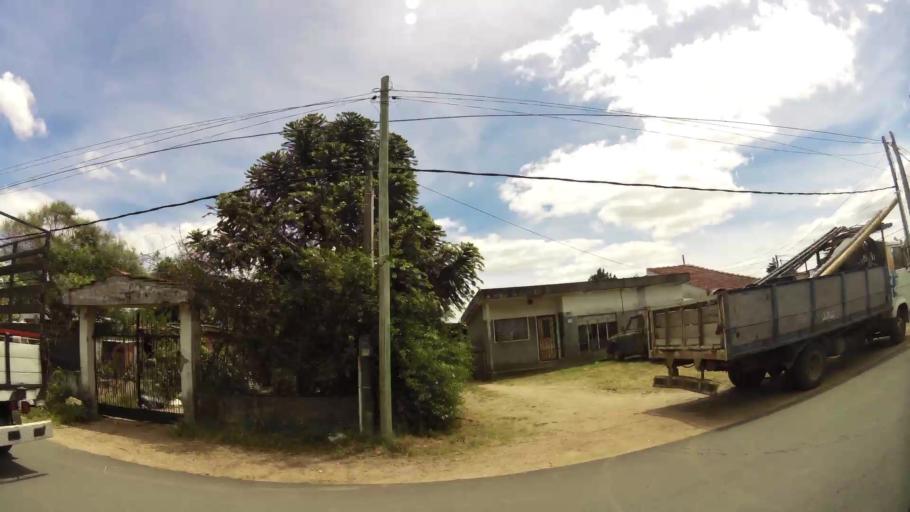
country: UY
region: Canelones
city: Colonia Nicolich
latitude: -34.8297
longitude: -55.9731
